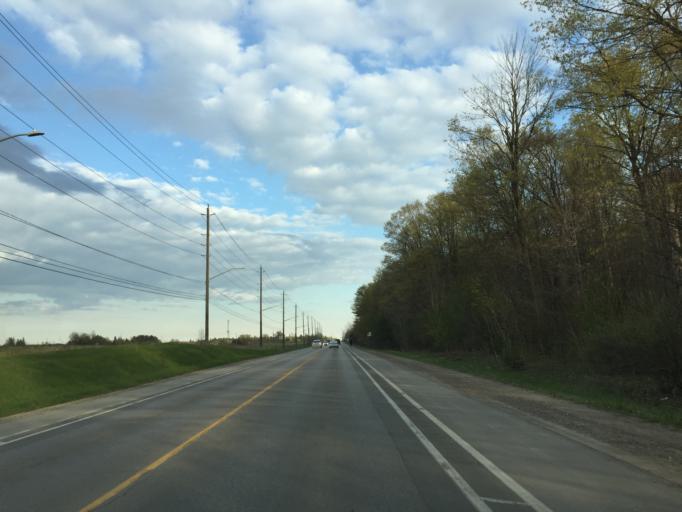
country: CA
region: Ontario
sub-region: Wellington County
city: Guelph
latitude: 43.5445
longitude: -80.2136
